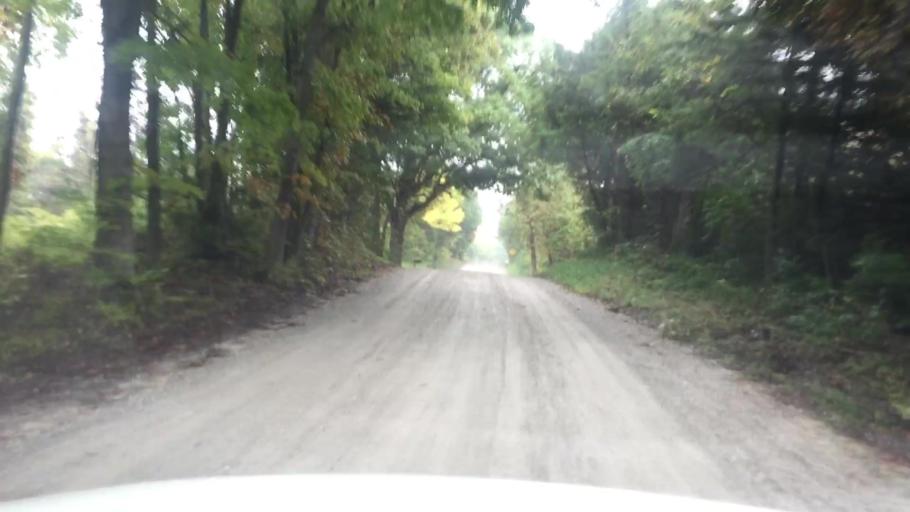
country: US
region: Missouri
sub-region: Boone County
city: Ashland
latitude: 38.8186
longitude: -92.2967
